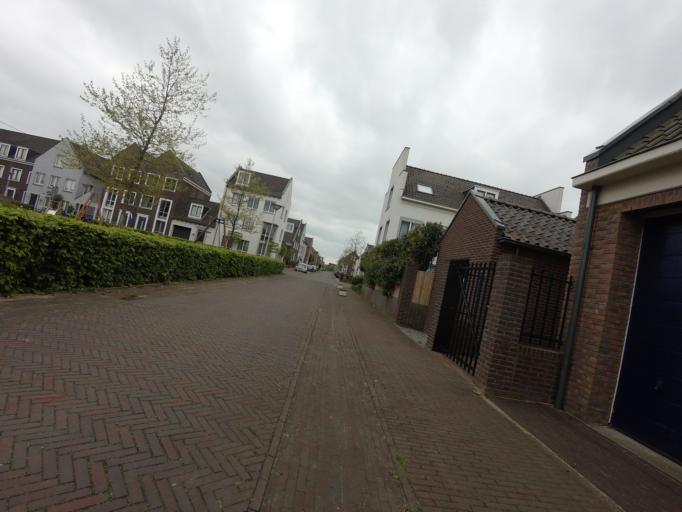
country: NL
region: Utrecht
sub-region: Stichtse Vecht
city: Maarssen
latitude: 52.0846
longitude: 5.0453
